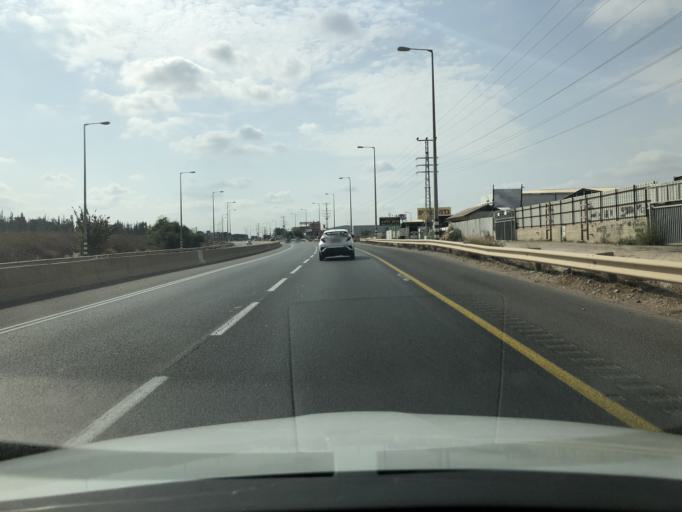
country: IL
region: Central District
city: Tirah
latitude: 32.2269
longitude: 34.9819
